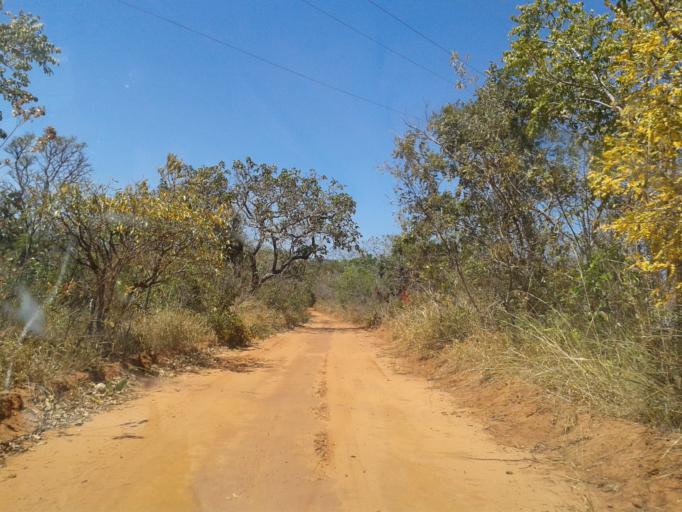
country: BR
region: Minas Gerais
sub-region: Monte Alegre De Minas
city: Monte Alegre de Minas
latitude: -18.8371
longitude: -49.0951
